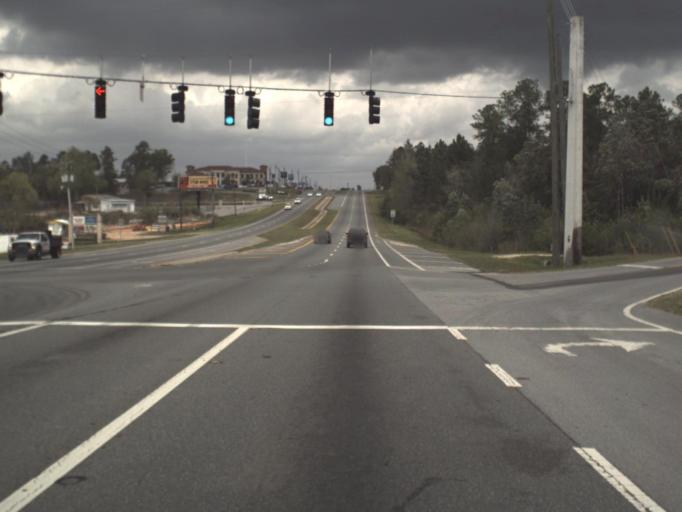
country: US
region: Florida
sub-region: Okaloosa County
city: Crestview
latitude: 30.7111
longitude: -86.5701
